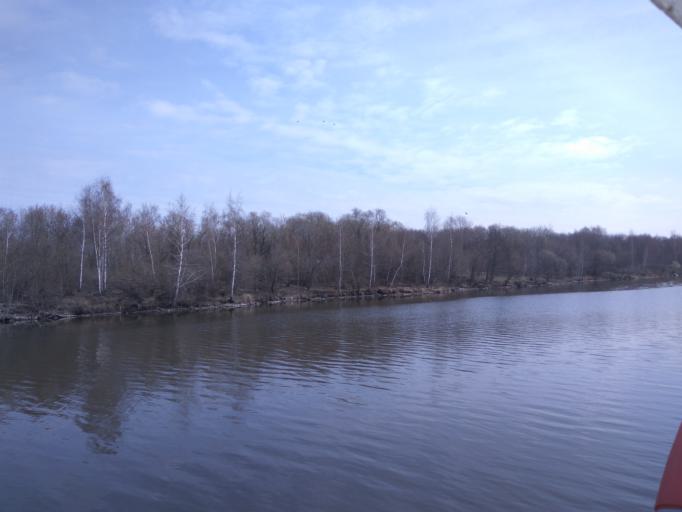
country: RU
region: Moscow
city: Kolomenskoye
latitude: 55.6915
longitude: 37.6979
